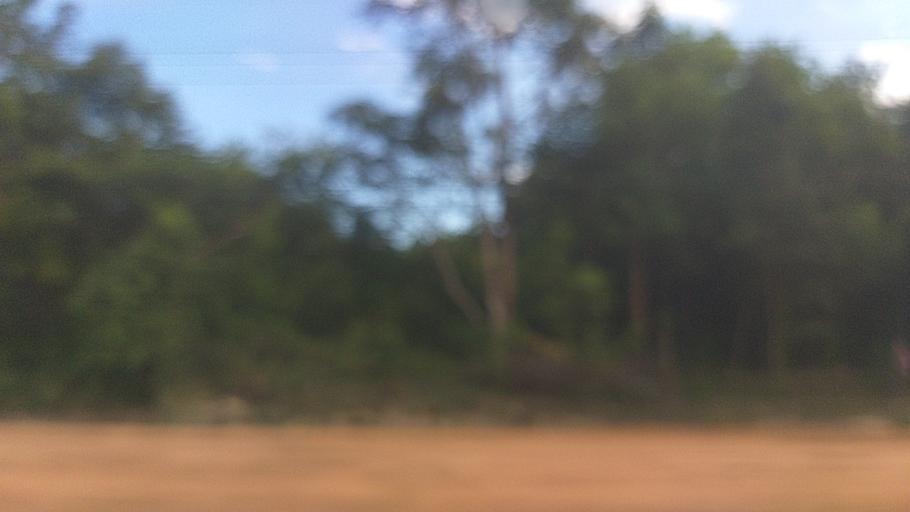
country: TH
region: Surin
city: Kap Choeng
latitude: 14.4691
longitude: 103.6229
